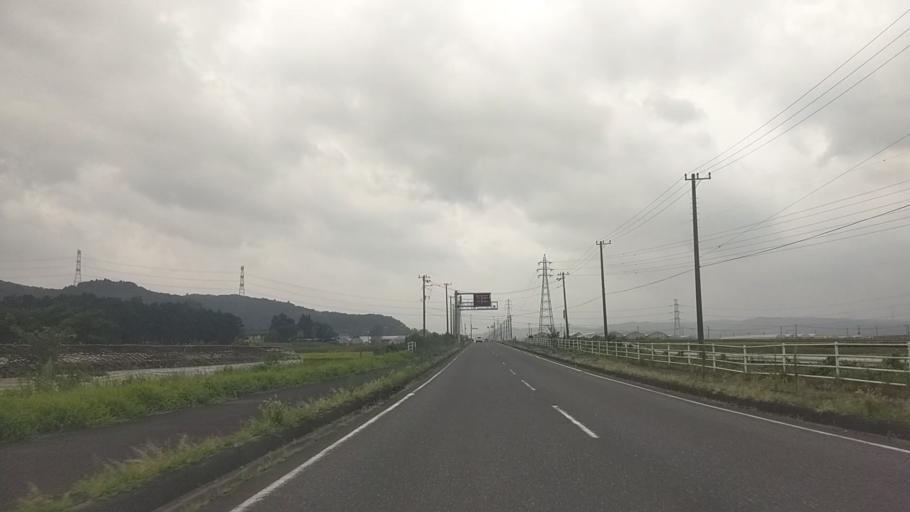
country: JP
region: Chiba
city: Kisarazu
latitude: 35.3530
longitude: 140.0548
